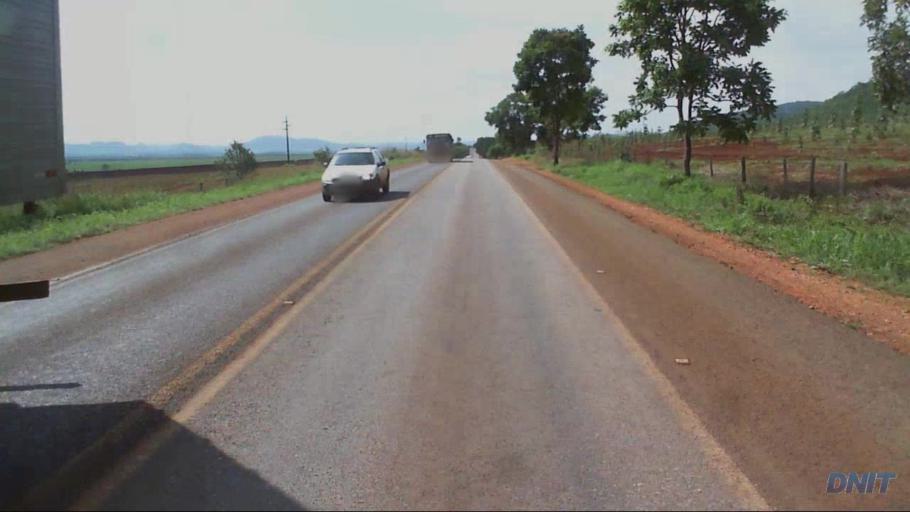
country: BR
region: Goias
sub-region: Barro Alto
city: Barro Alto
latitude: -14.9943
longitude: -48.9072
